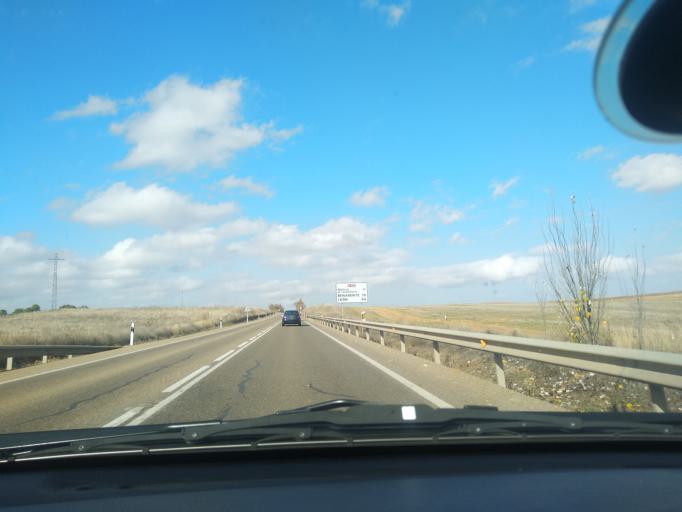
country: ES
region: Castille and Leon
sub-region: Provincia de Valladolid
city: Medina de Rioseco
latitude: 41.8960
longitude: -5.0574
